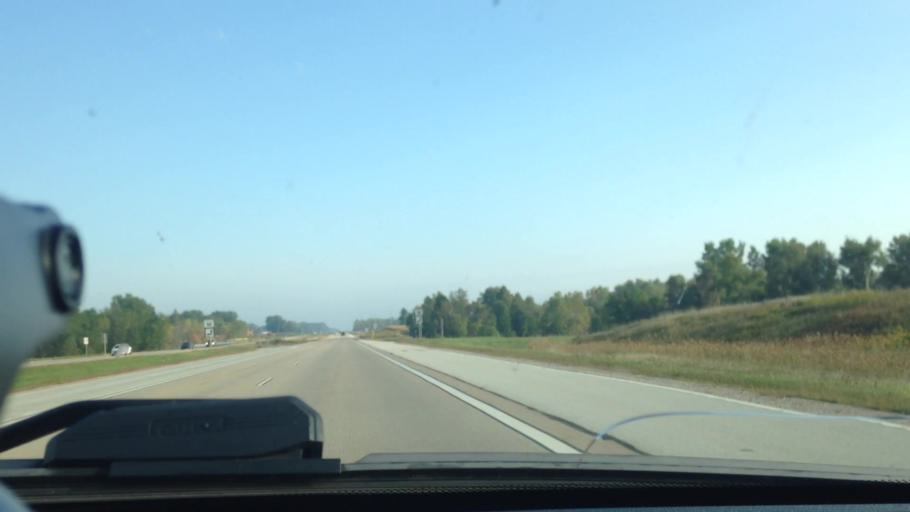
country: US
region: Wisconsin
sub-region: Oconto County
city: Oconto Falls
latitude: 45.0074
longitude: -88.0450
